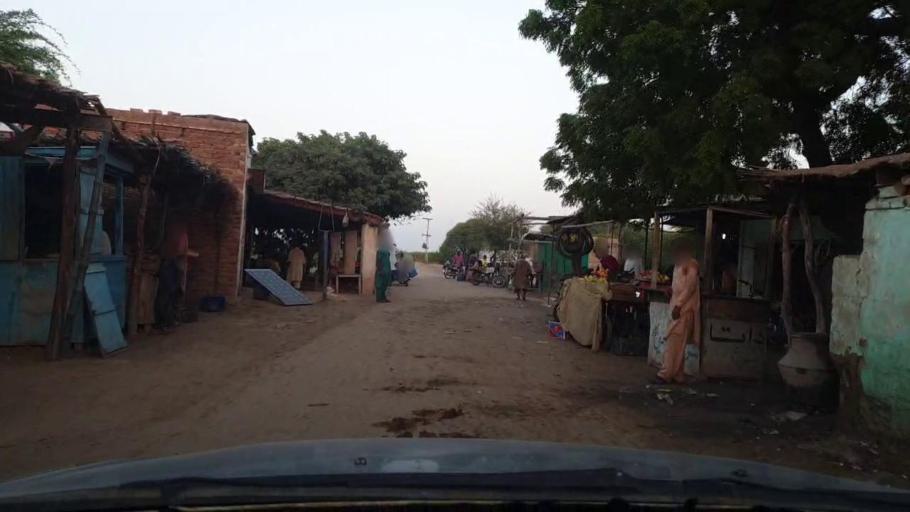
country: PK
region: Sindh
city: Tando Ghulam Ali
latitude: 25.0658
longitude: 68.9491
